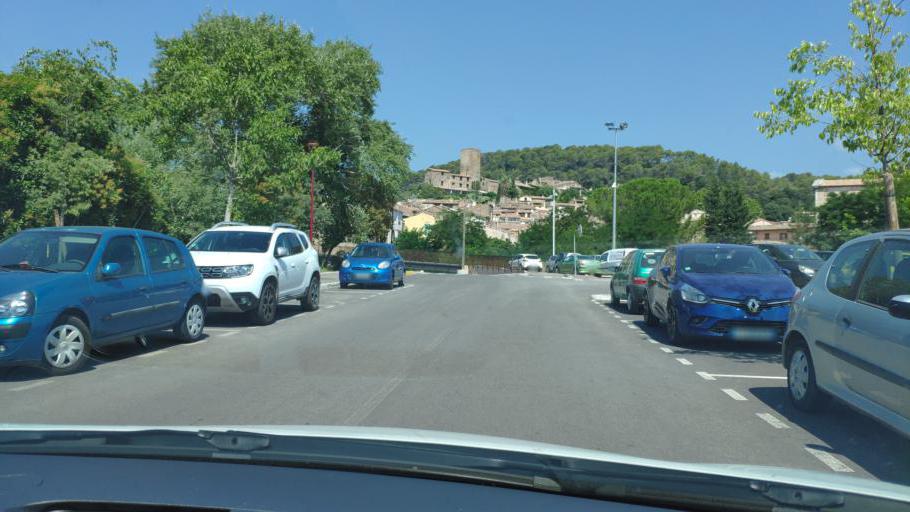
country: FR
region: Provence-Alpes-Cote d'Azur
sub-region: Departement du Var
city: Les Arcs
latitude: 43.4625
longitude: 6.4807
